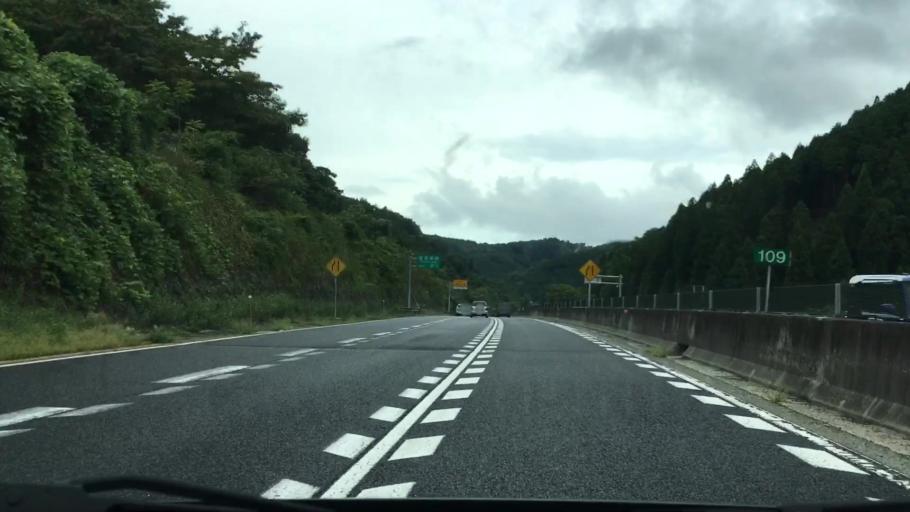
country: JP
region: Hyogo
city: Yamazakicho-nakabirose
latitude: 35.0429
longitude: 134.4666
